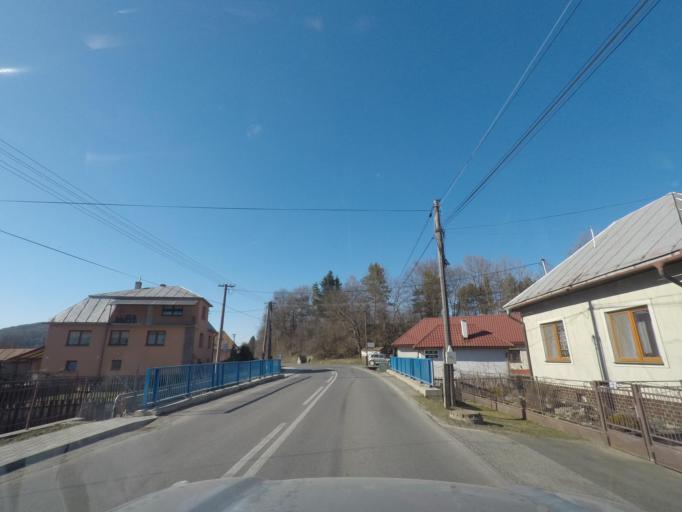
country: SK
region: Presovsky
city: Snina
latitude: 48.9960
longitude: 22.2354
